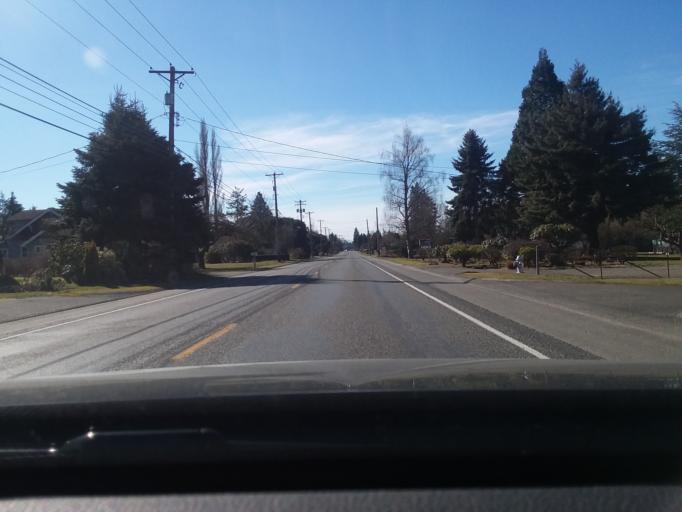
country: US
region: Washington
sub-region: Pierce County
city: Midland
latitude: 47.1670
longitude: -122.3890
